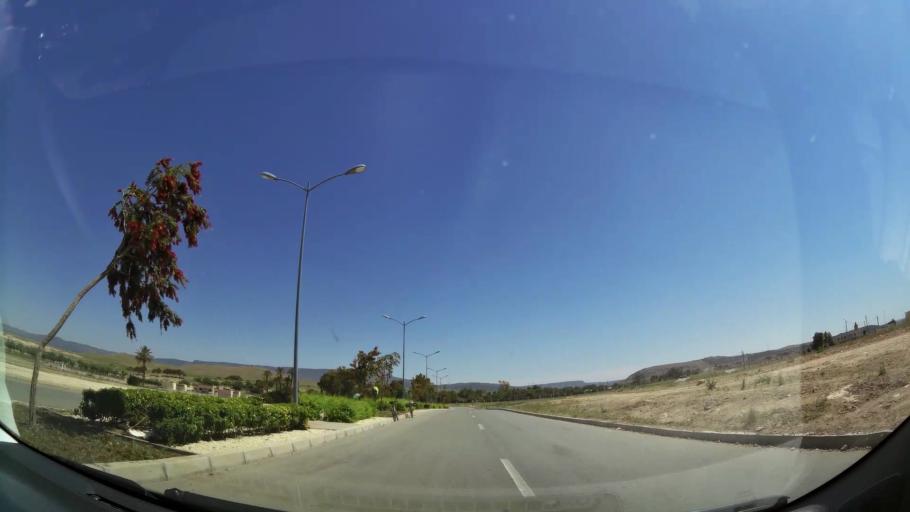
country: MA
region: Oriental
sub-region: Oujda-Angad
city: Oujda
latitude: 34.6700
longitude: -1.8649
